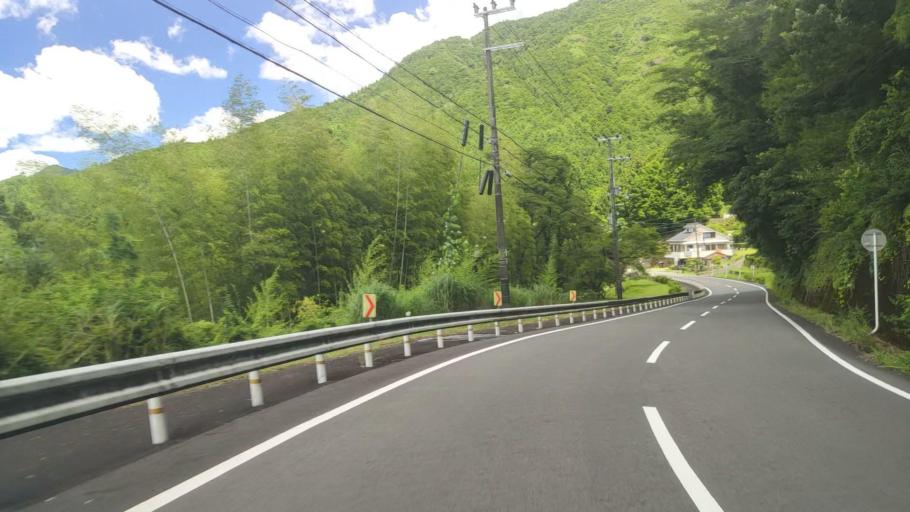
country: JP
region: Mie
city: Owase
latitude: 33.9559
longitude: 136.0691
